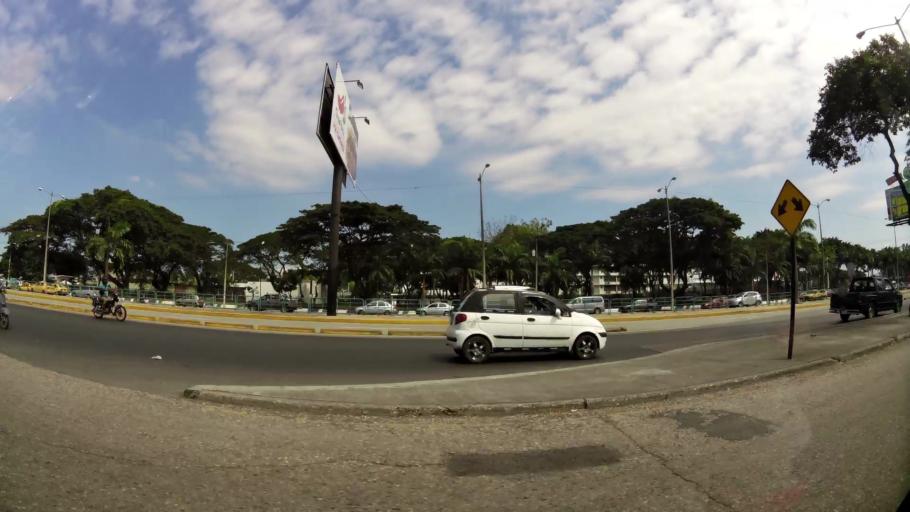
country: EC
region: Guayas
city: Guayaquil
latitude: -2.2335
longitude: -79.8969
